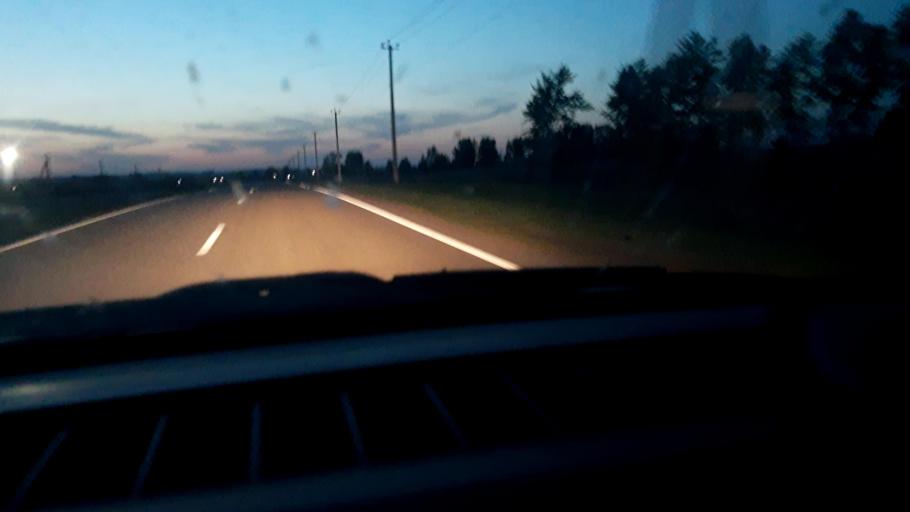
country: RU
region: Bashkortostan
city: Asanovo
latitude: 54.8368
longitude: 55.4600
